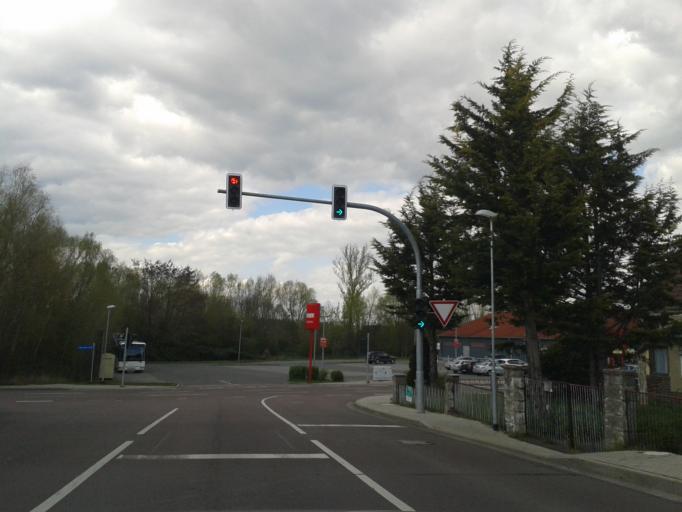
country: DE
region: Saxony-Anhalt
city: Teutschenthal
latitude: 51.4539
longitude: 11.8171
